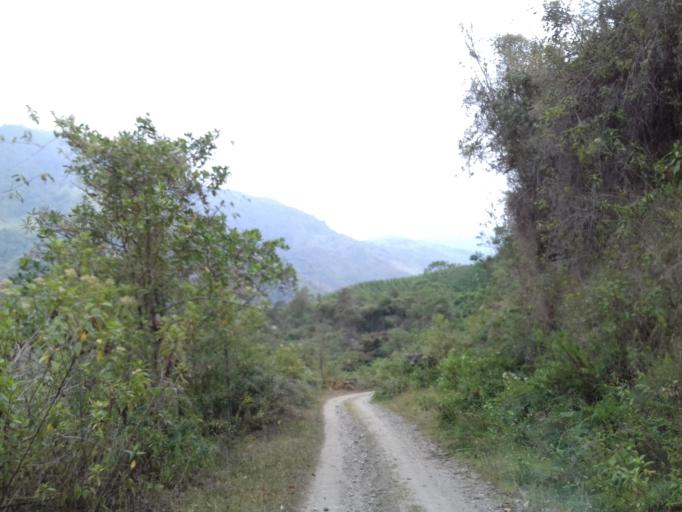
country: CO
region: Tolima
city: Cajamarca
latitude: 4.5321
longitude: -75.4144
